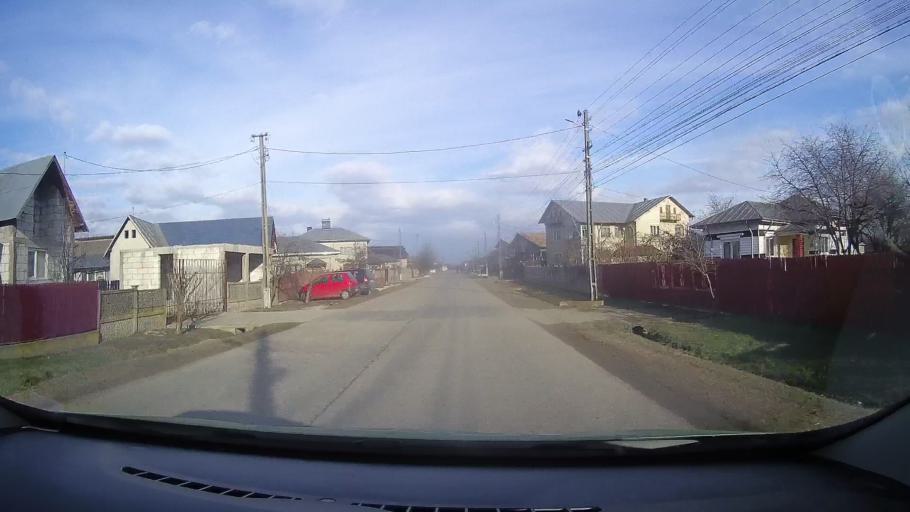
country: RO
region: Dambovita
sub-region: Comuna Vacaresti
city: Vacaresti
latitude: 44.8570
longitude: 25.4877
